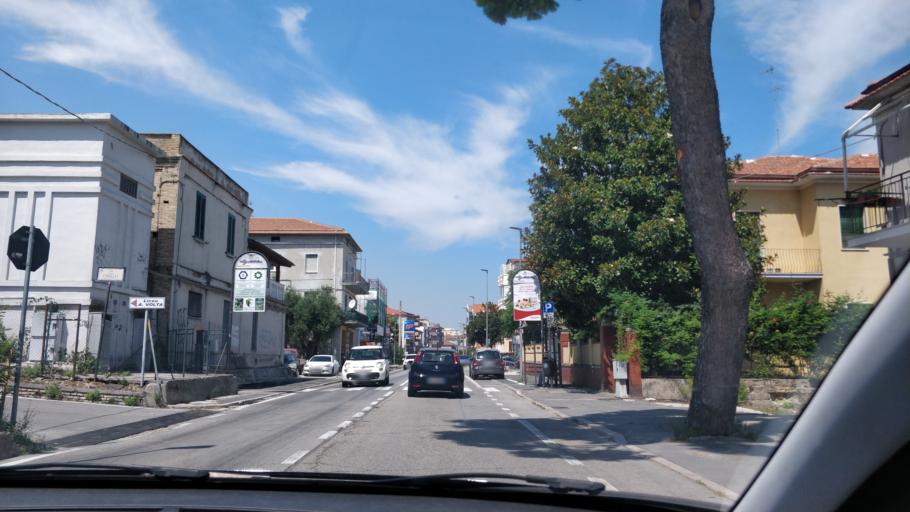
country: IT
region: Abruzzo
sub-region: Provincia di Chieti
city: Francavilla al Mare
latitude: 42.4153
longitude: 14.2980
